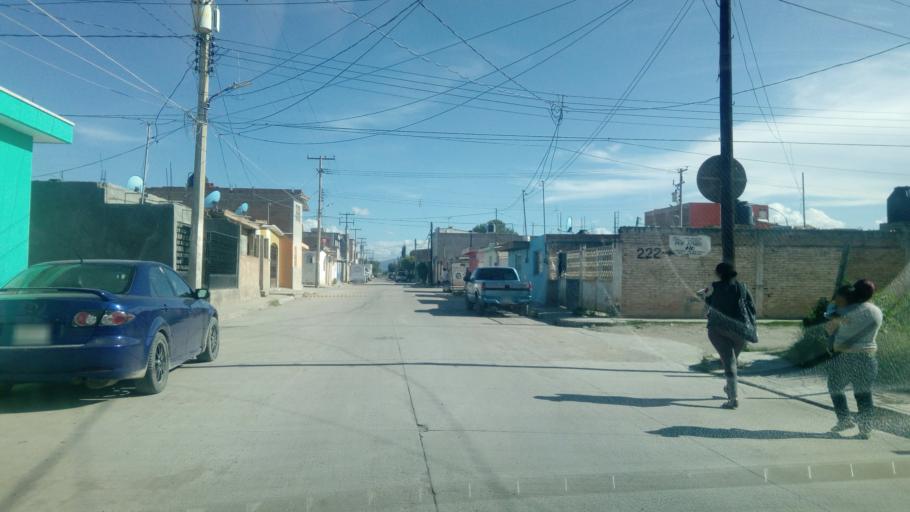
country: MX
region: Durango
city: Victoria de Durango
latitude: 24.0095
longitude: -104.6265
